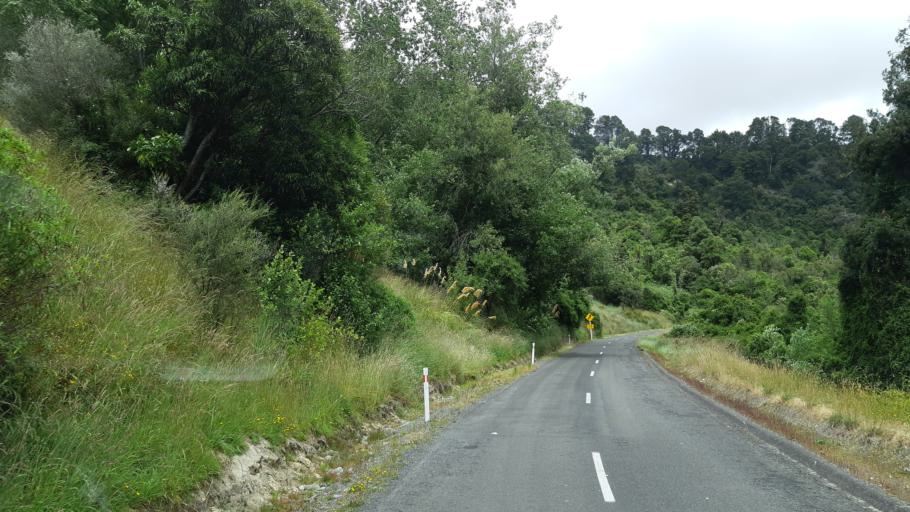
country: NZ
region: Manawatu-Wanganui
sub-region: Palmerston North City
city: Palmerston North
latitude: -39.9381
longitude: 175.9214
